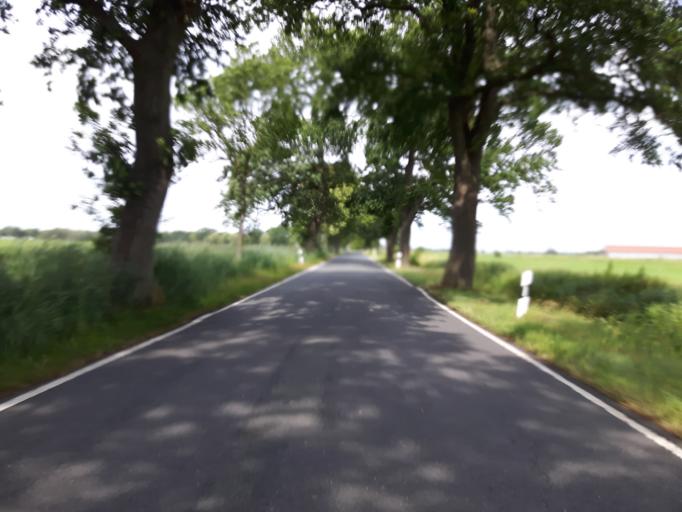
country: DE
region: Lower Saxony
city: Rastede
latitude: 53.3359
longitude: 8.2522
